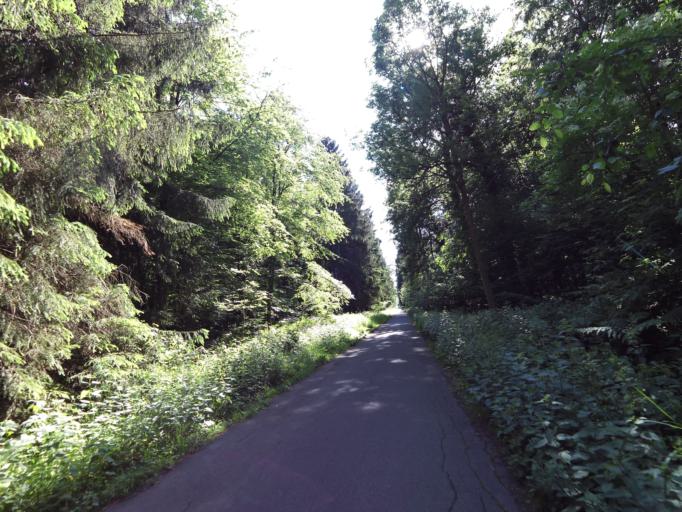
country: DE
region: North Rhine-Westphalia
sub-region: Regierungsbezirk Koln
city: Wachtberg
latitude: 50.6761
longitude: 7.1057
